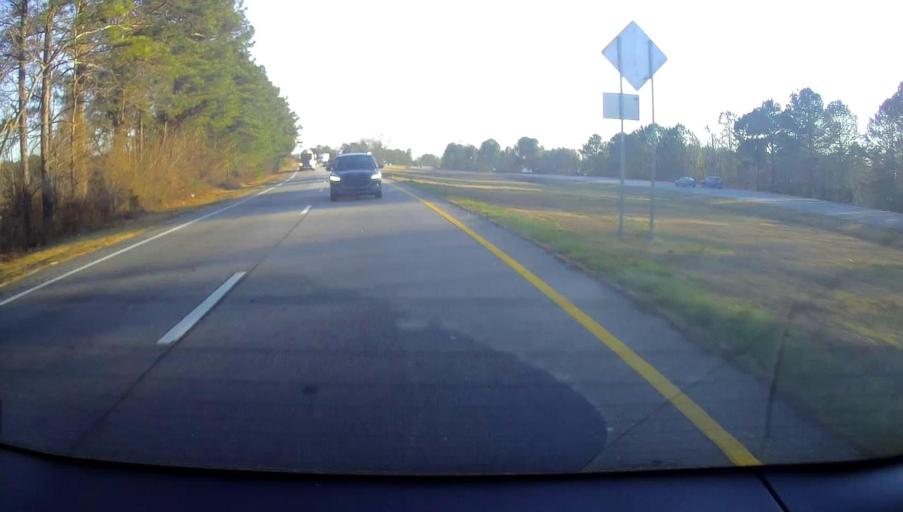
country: US
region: Georgia
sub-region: Fayette County
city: Tyrone
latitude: 33.5053
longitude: -84.5770
